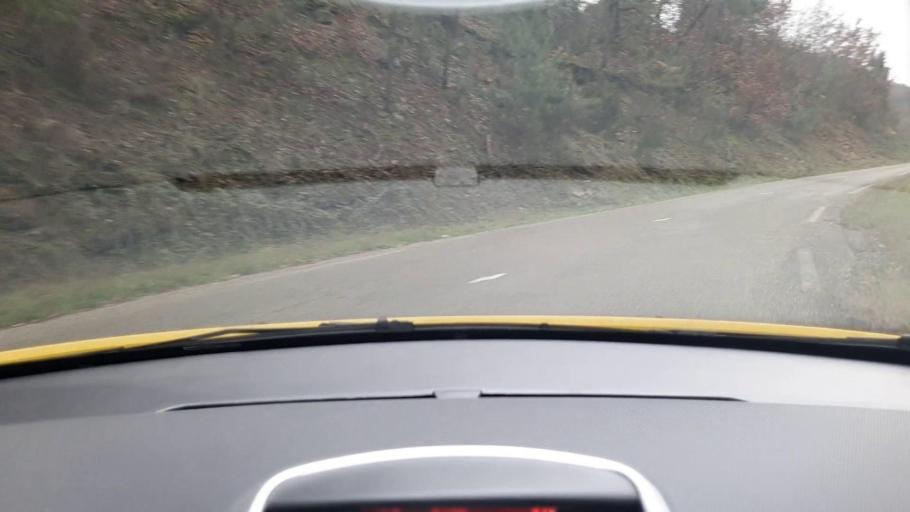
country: FR
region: Languedoc-Roussillon
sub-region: Departement du Gard
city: Besseges
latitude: 44.3149
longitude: 4.1382
